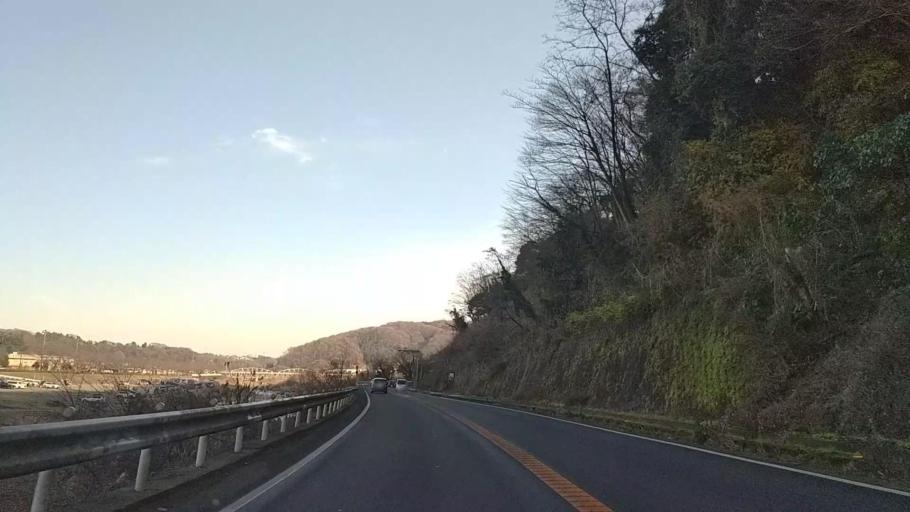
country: JP
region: Kanagawa
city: Zama
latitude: 35.5233
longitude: 139.2850
